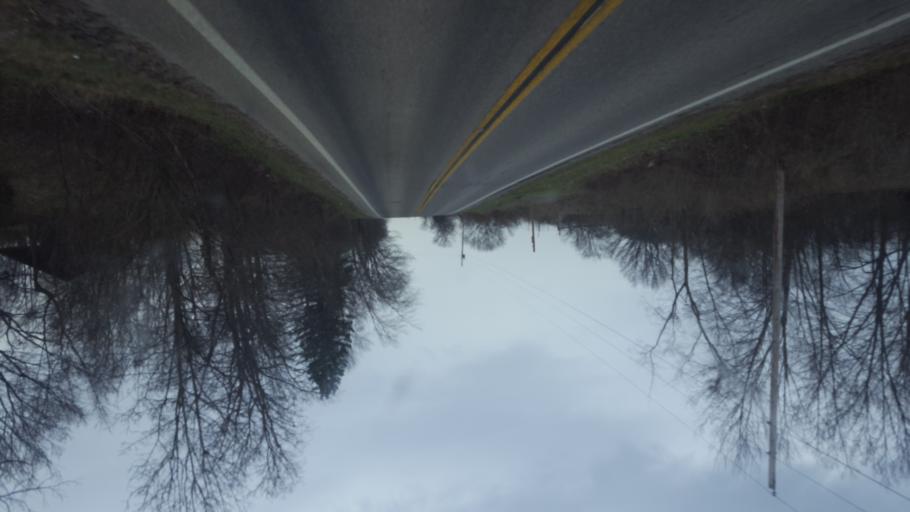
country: US
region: Ohio
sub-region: Morrow County
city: Mount Gilead
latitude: 40.4909
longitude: -82.8202
